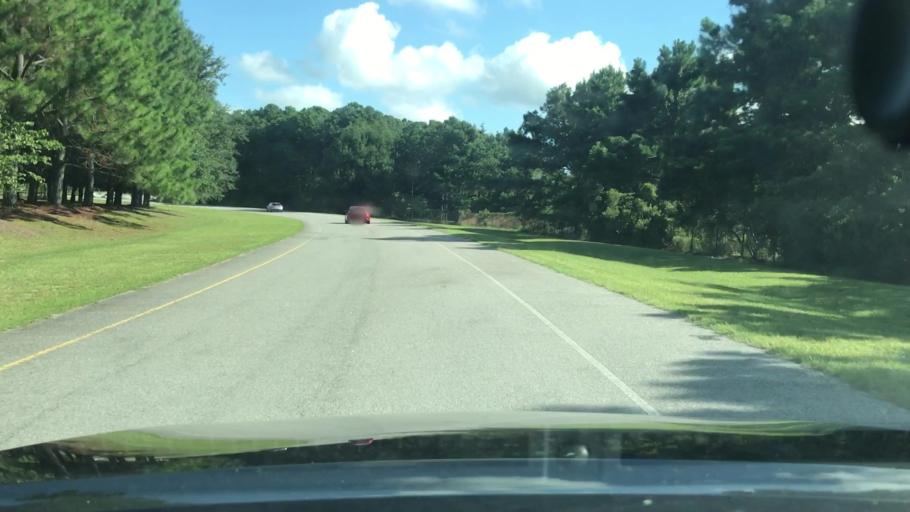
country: US
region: South Carolina
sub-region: Beaufort County
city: Hilton Head Island
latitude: 32.2129
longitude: -80.7374
